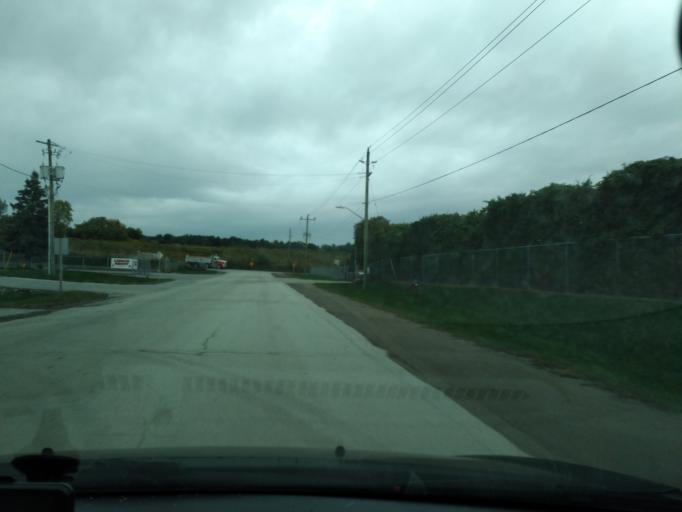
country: CA
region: Ontario
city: Bradford West Gwillimbury
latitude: 44.1409
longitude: -79.5563
